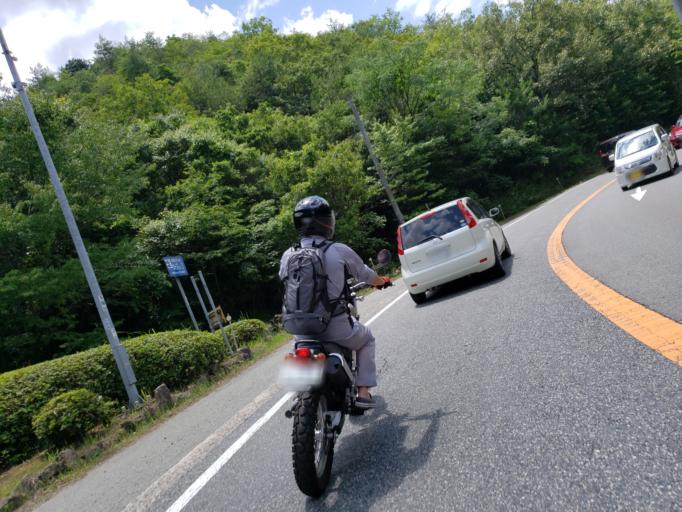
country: JP
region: Hyogo
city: Aioi
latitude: 34.7985
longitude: 134.4499
